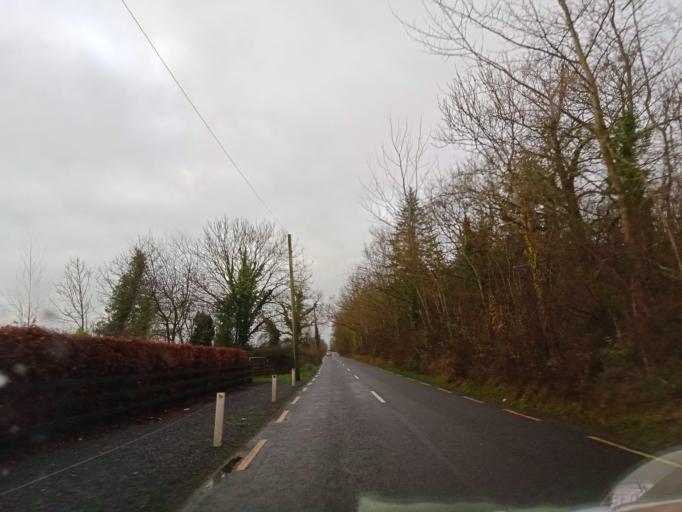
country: IE
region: Leinster
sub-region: Kilkenny
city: Callan
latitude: 52.5767
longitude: -7.3647
